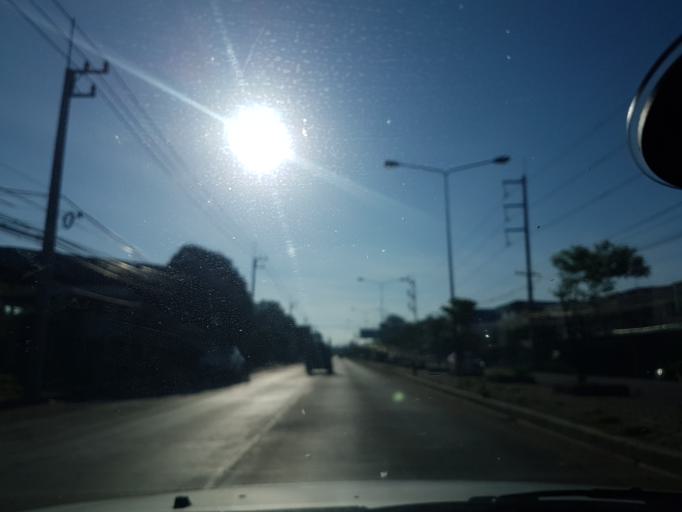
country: TH
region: Lop Buri
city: Lop Buri
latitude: 14.7743
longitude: 100.6976
